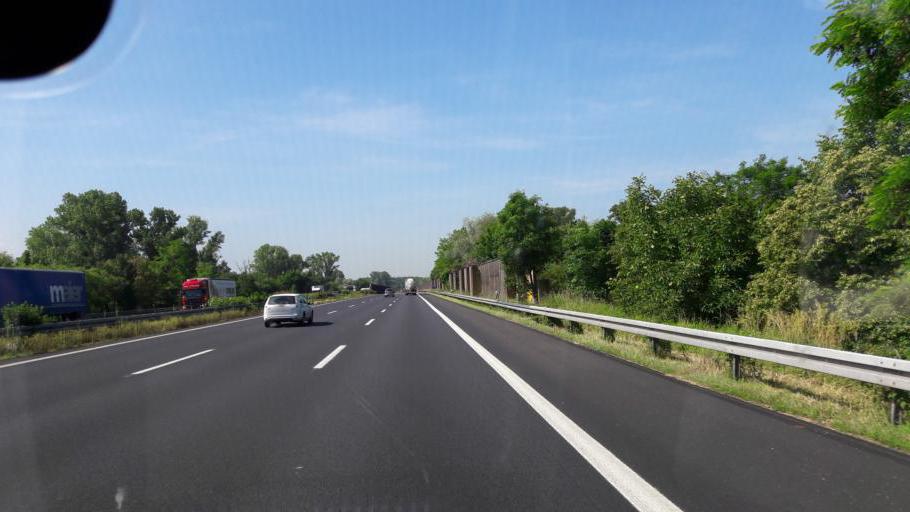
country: DE
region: Baden-Wuerttemberg
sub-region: Karlsruhe Region
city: Rastatt
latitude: 48.8438
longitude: 8.2301
